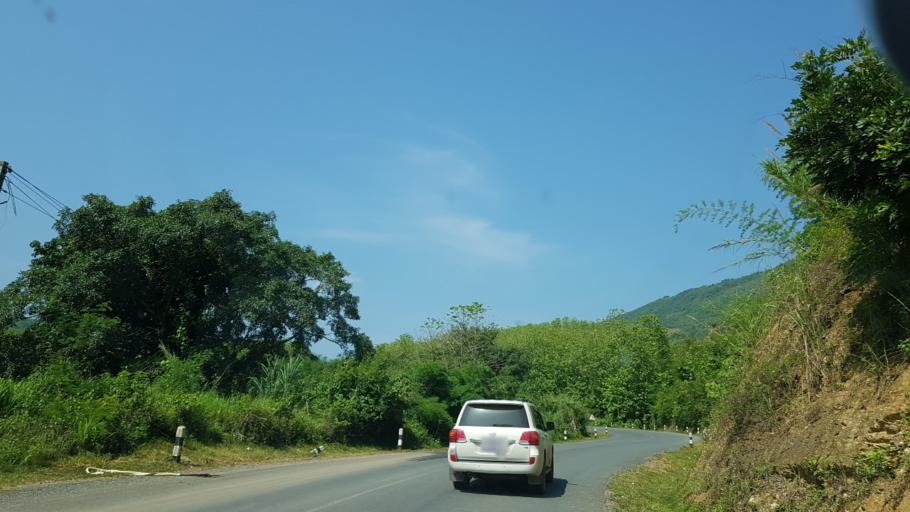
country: LA
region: Louangphabang
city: Xiang Ngeun
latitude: 19.7246
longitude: 102.1516
